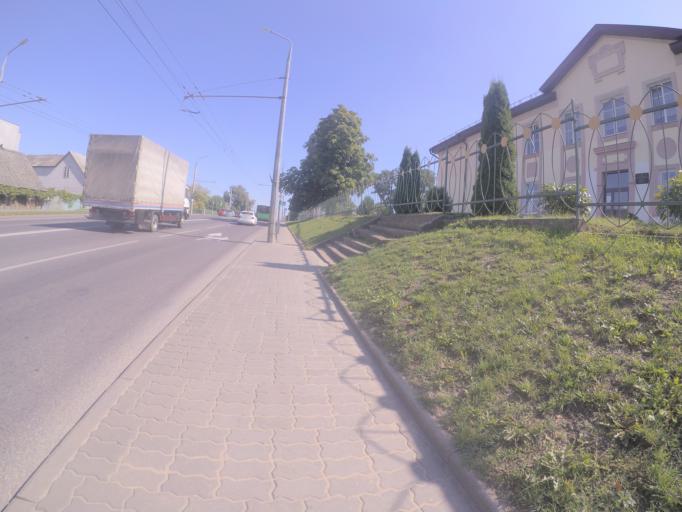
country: BY
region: Grodnenskaya
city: Hrodna
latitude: 53.6705
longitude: 23.8127
